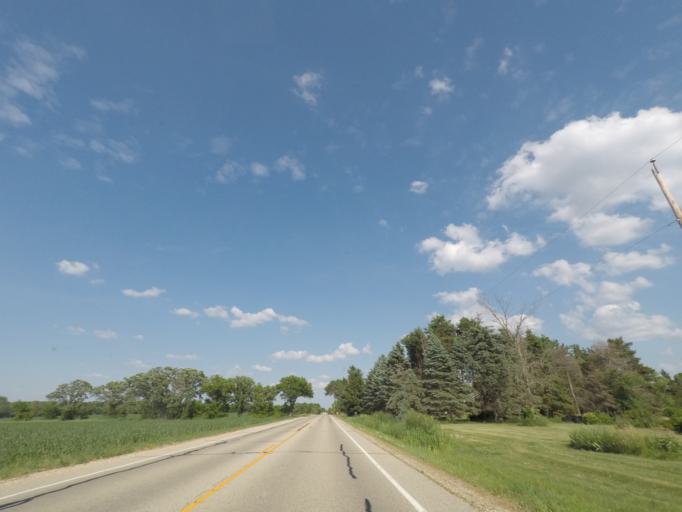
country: US
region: Wisconsin
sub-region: Waukesha County
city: Eagle
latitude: 42.7931
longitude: -88.5154
